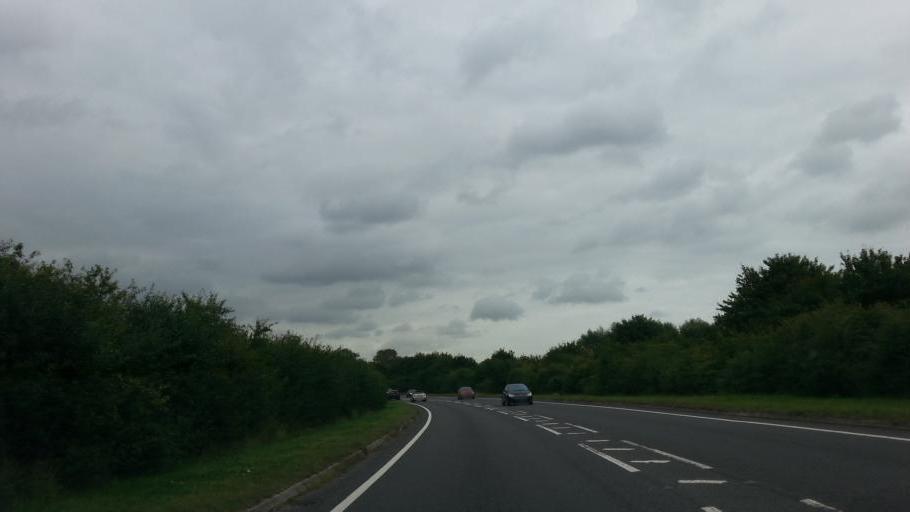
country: GB
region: England
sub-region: Essex
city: Chelmsford
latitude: 51.7529
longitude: 0.4817
